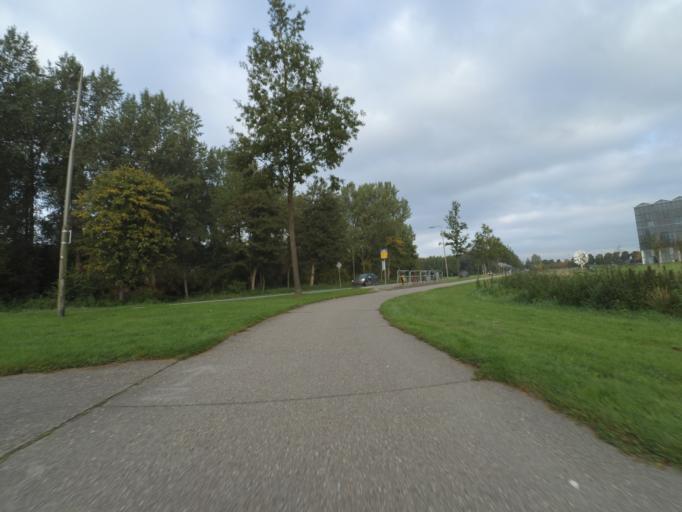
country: NL
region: Flevoland
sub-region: Gemeente Dronten
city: Dronten
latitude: 52.5273
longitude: 5.6948
